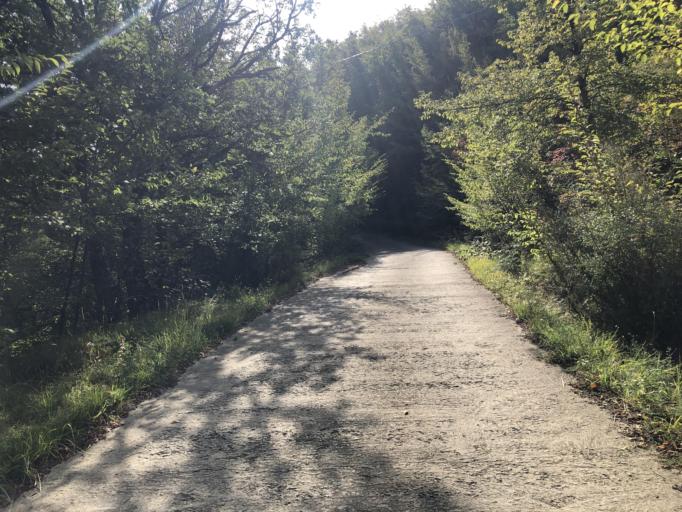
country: IT
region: Emilia-Romagna
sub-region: Forli-Cesena
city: Portico e San Benedetto
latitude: 44.0159
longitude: 11.7850
